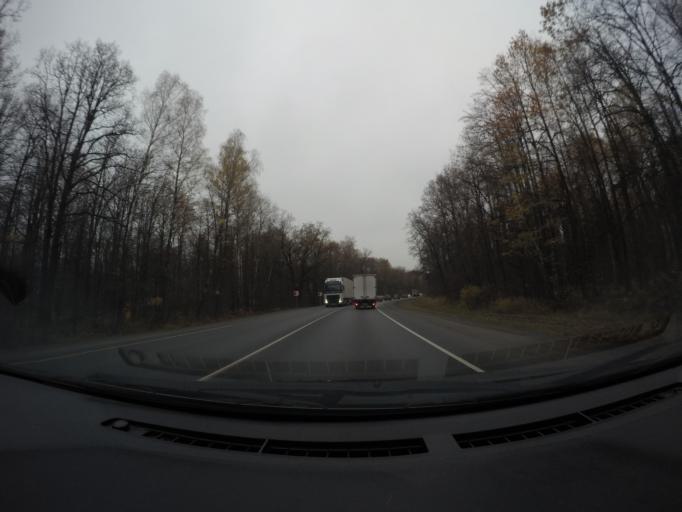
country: RU
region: Moskovskaya
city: Bronnitsy
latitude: 55.3969
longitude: 38.2225
